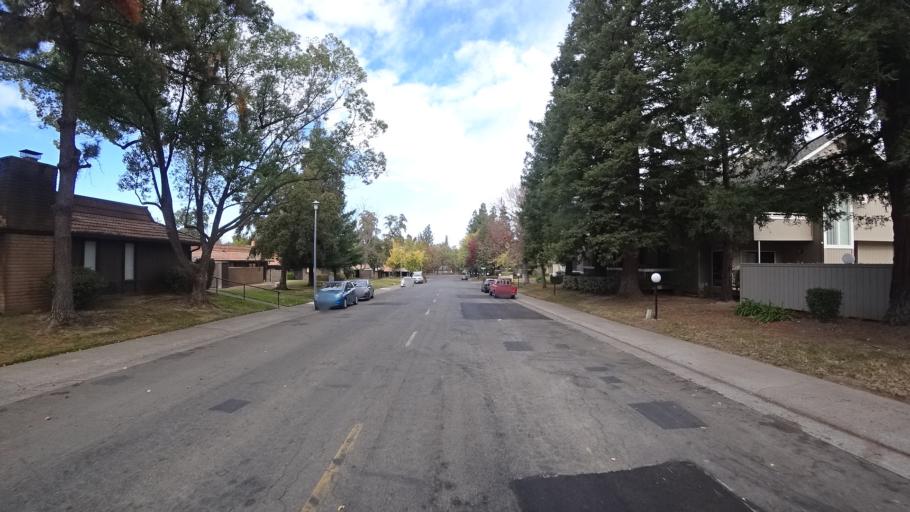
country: US
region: California
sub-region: Sacramento County
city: Fair Oaks
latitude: 38.6655
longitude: -121.2666
